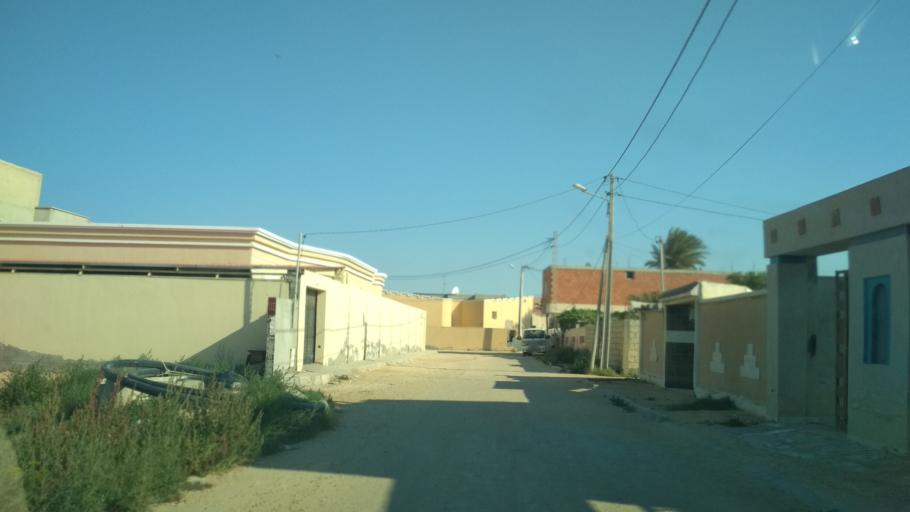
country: TN
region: Qabis
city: Gabes
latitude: 33.9499
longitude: 10.0641
